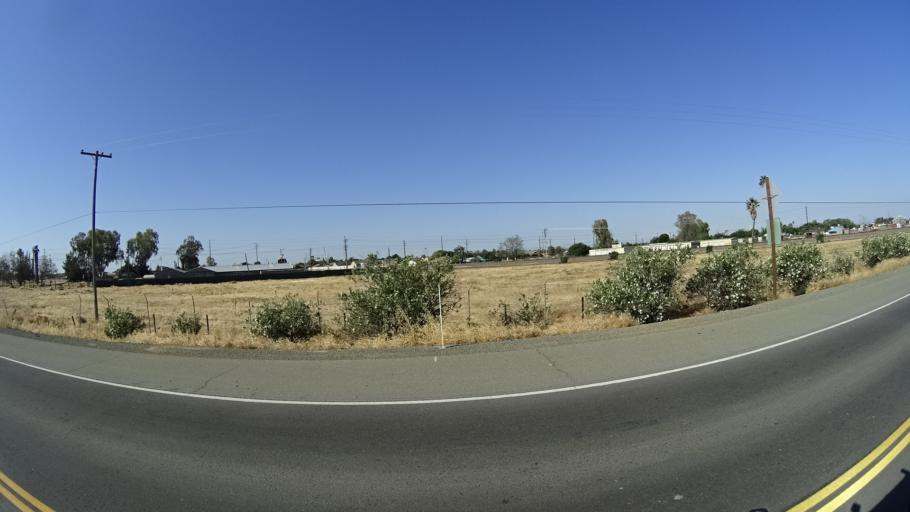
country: US
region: California
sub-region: Kings County
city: Corcoran
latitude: 36.1110
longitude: -119.5644
